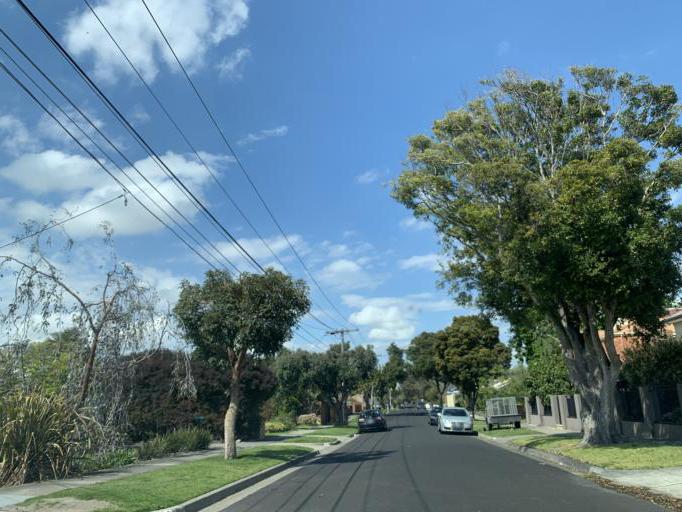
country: AU
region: Victoria
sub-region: Kingston
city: Mordialloc
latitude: -37.9981
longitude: 145.0900
